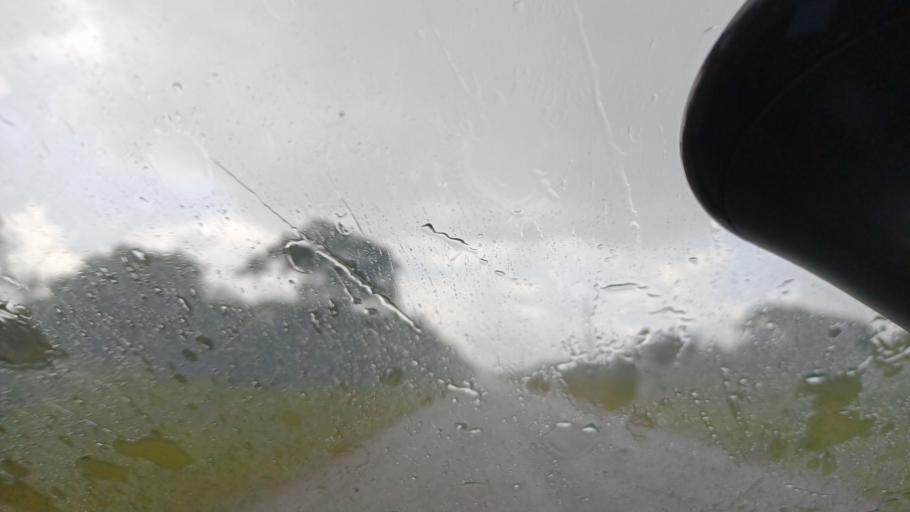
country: ZM
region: North-Western
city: Kasempa
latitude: -13.0951
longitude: 25.9144
